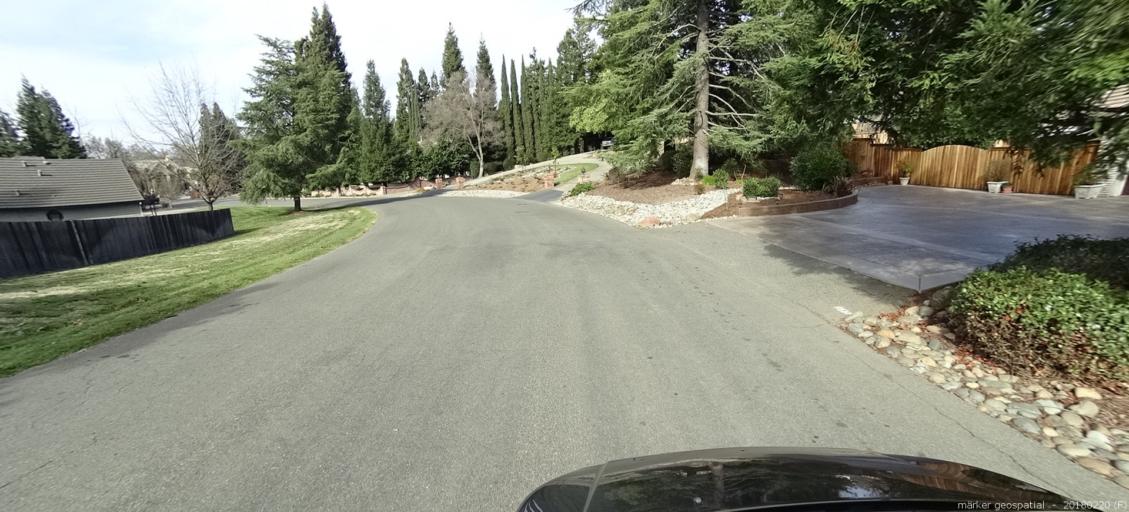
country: US
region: California
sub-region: Sacramento County
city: Orangevale
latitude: 38.7121
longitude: -121.2385
